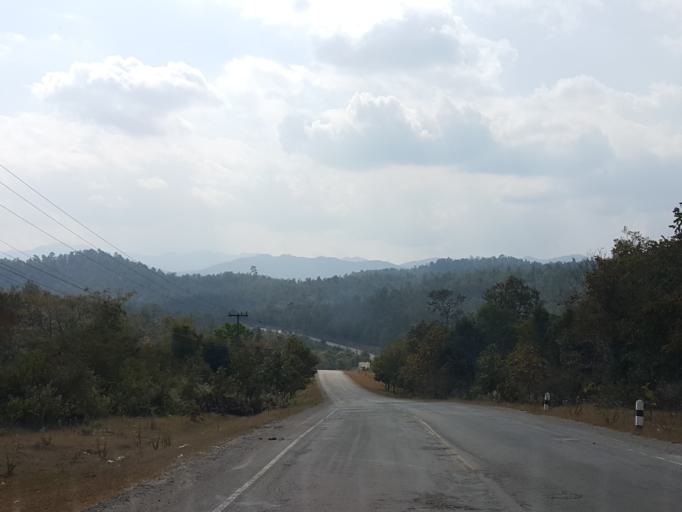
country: TH
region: Chiang Mai
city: Om Koi
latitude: 17.8294
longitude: 98.3643
